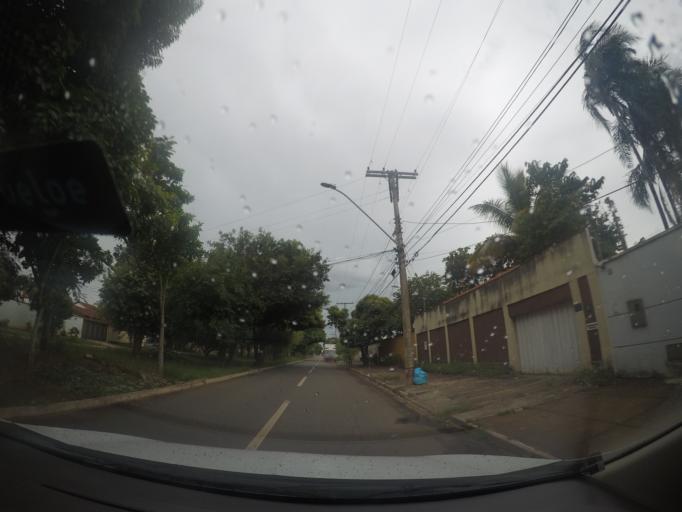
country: BR
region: Goias
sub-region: Goiania
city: Goiania
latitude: -16.6422
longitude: -49.2339
